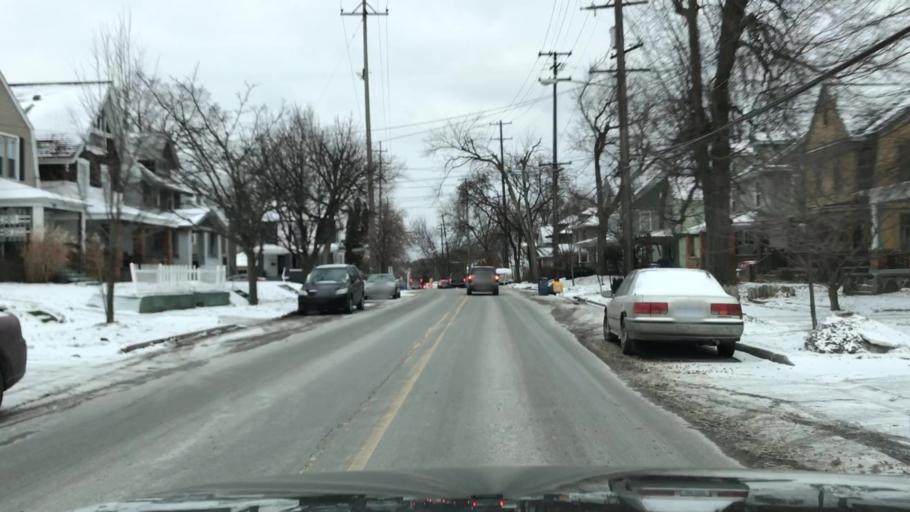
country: US
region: Michigan
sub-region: Kent County
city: Grand Rapids
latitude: 42.9604
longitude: -85.6397
